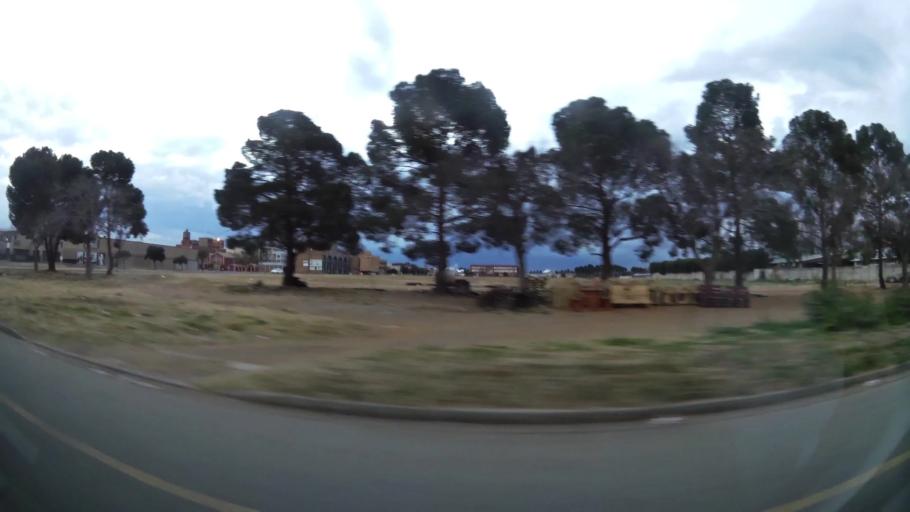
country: ZA
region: Orange Free State
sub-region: Lejweleputswa District Municipality
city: Welkom
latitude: -27.9788
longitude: 26.7436
